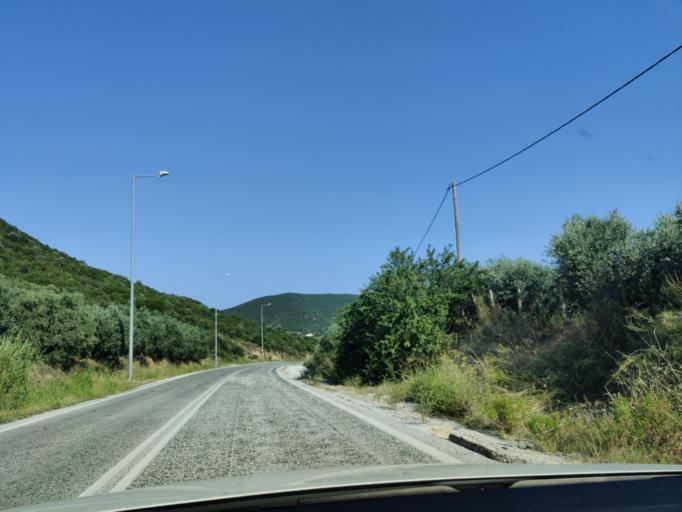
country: GR
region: East Macedonia and Thrace
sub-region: Nomos Kavalas
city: Nea Iraklitsa
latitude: 40.8589
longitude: 24.3059
